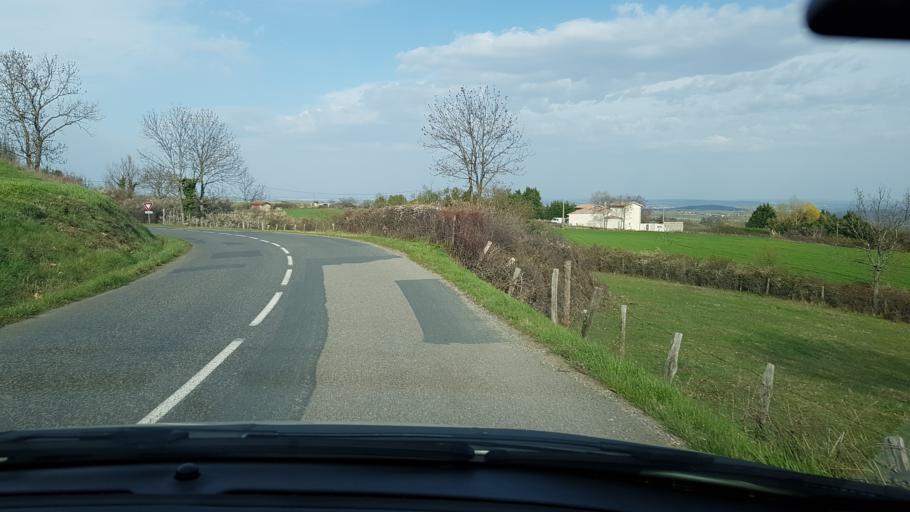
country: FR
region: Rhone-Alpes
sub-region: Departement du Rhone
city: Saint-Maurice-sur-Dargoire
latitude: 45.5855
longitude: 4.6415
